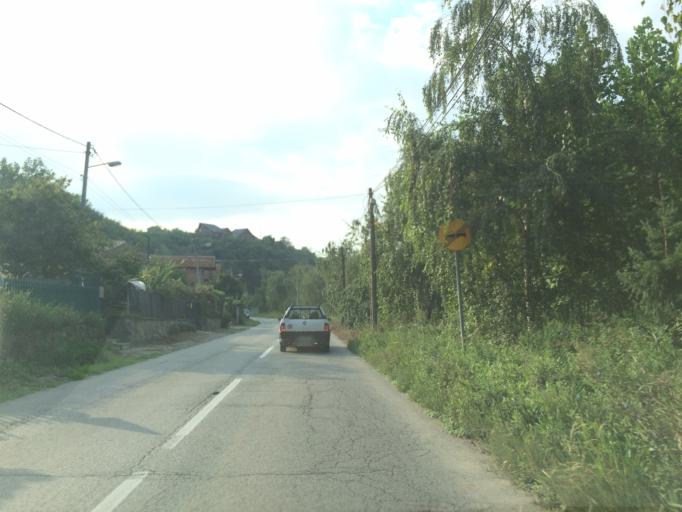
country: RS
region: Autonomna Pokrajina Vojvodina
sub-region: Juznobacki Okrug
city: Novi Sad
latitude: 45.2142
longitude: 19.8068
